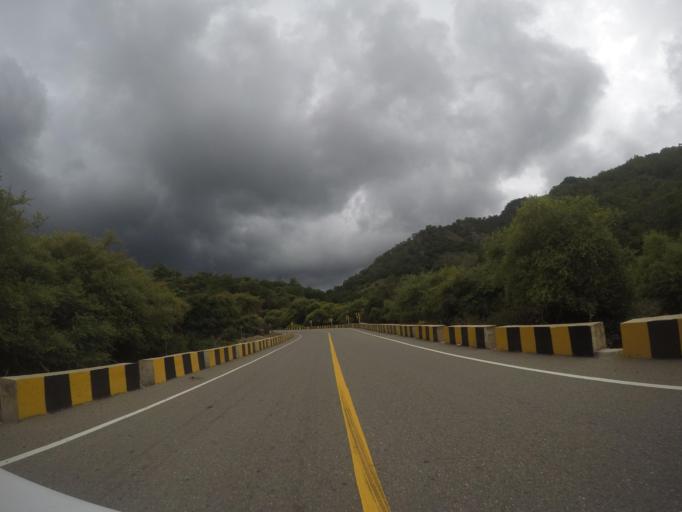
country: TL
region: Bobonaro
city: Maliana
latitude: -8.8436
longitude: 125.0603
